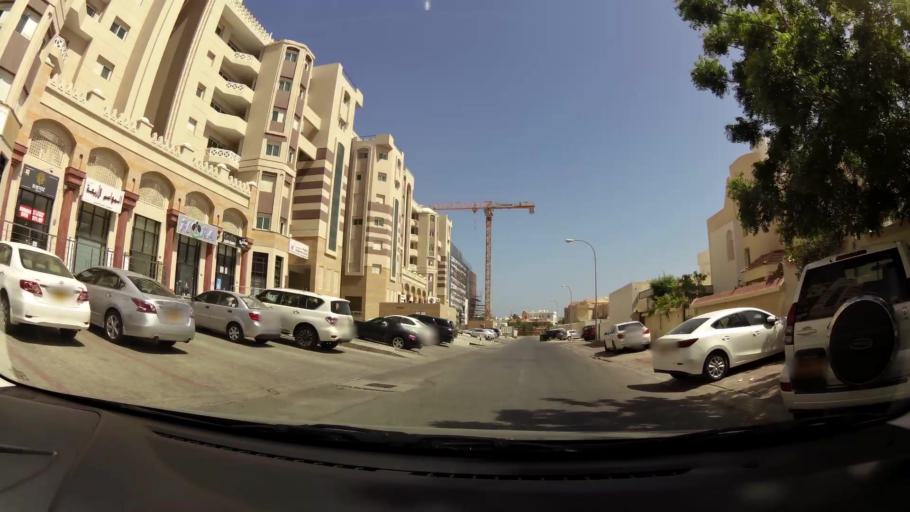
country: OM
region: Muhafazat Masqat
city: Bawshar
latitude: 23.5936
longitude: 58.4040
